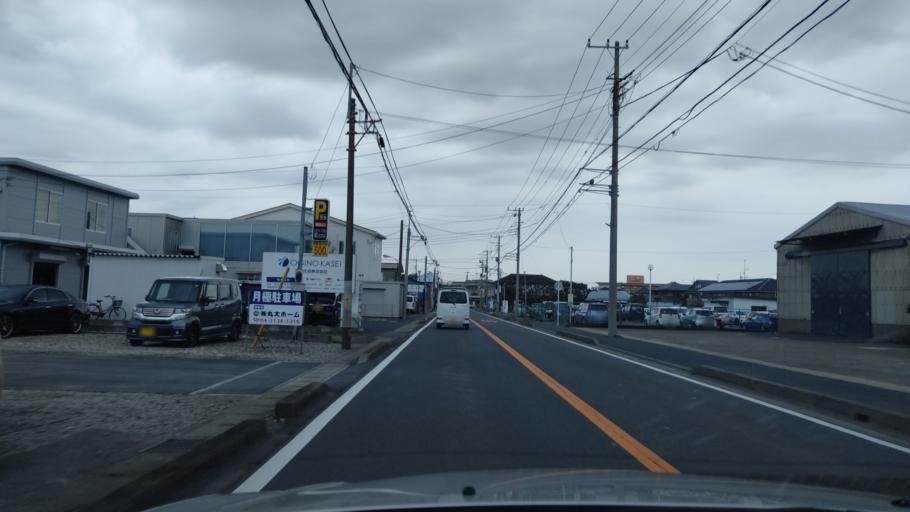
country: JP
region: Ibaraki
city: Moriya
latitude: 35.9125
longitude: 139.9490
